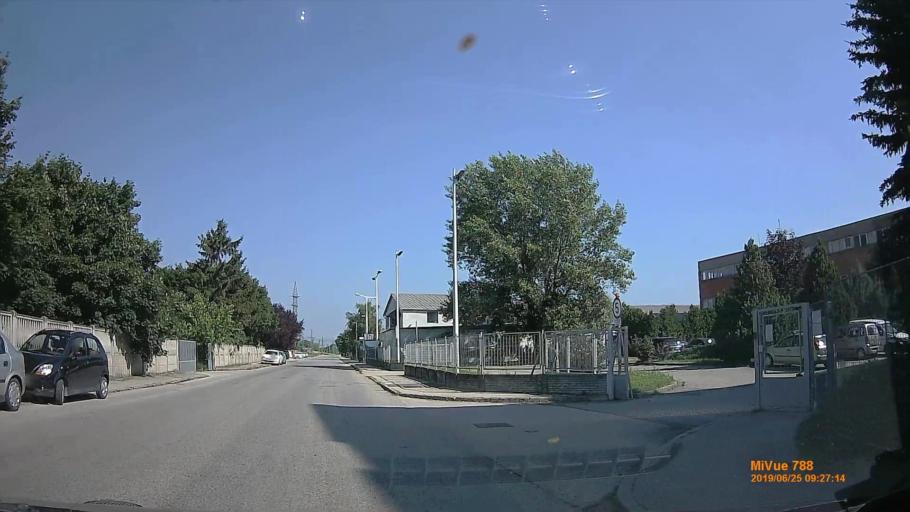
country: HU
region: Komarom-Esztergom
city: Esztergom
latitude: 47.7713
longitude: 18.7454
